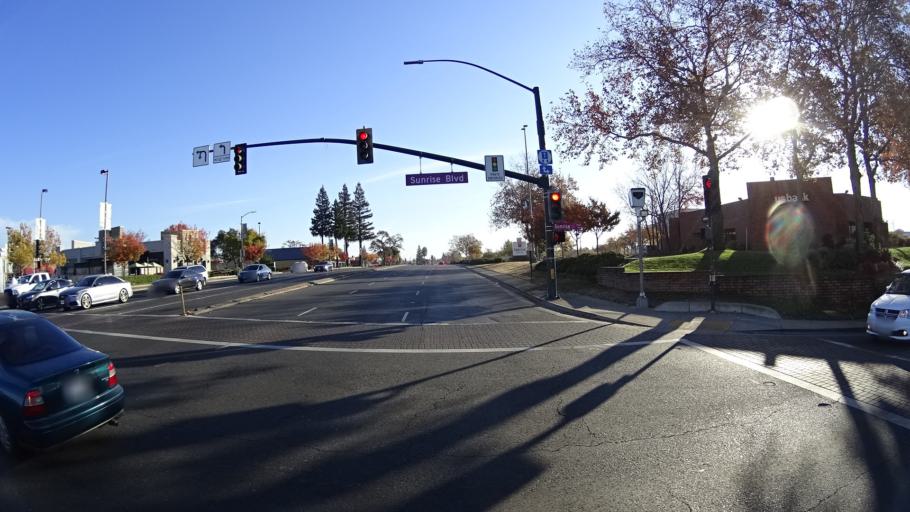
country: US
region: California
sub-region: Sacramento County
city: Citrus Heights
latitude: 38.6783
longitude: -121.2714
